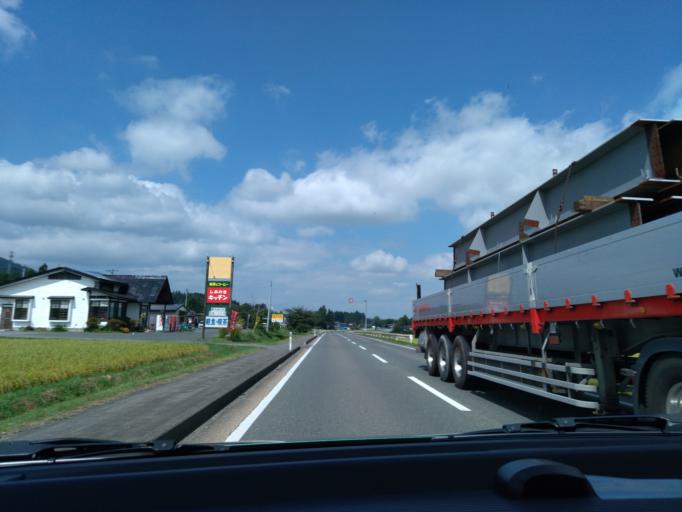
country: JP
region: Iwate
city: Hanamaki
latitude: 39.5185
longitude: 141.1102
